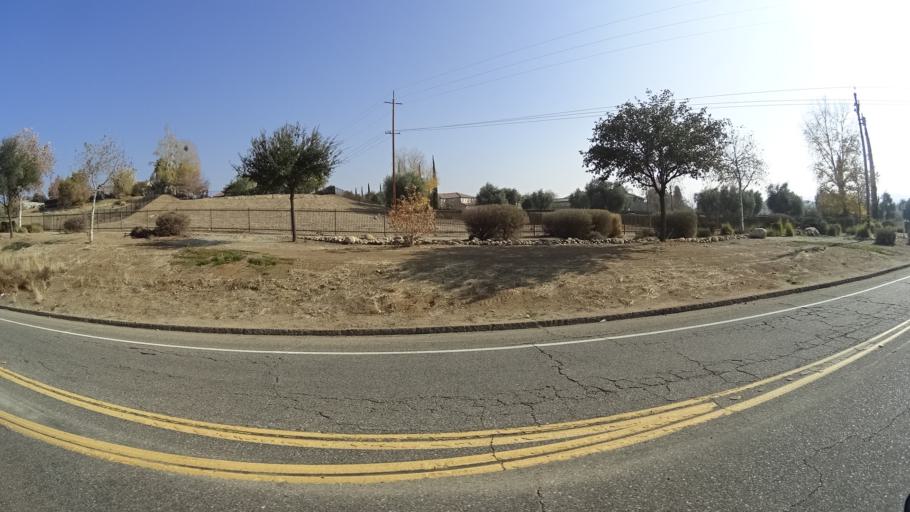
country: US
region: California
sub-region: Kern County
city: Oildale
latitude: 35.4131
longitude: -118.8599
